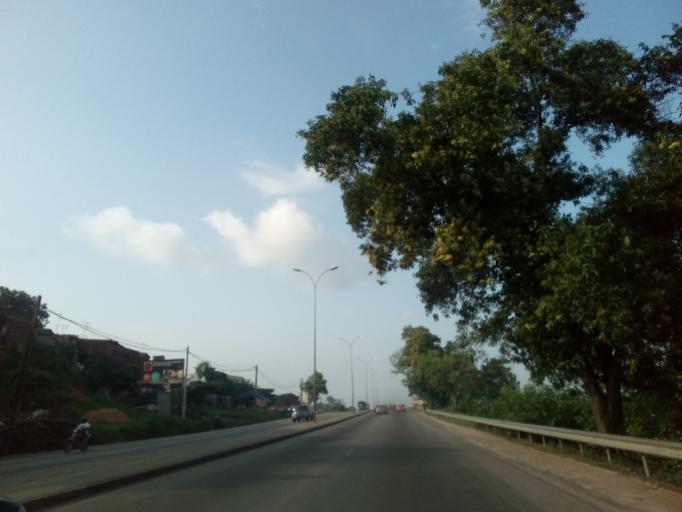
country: CI
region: Lagunes
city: Abidjan
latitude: 5.3501
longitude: -4.0400
